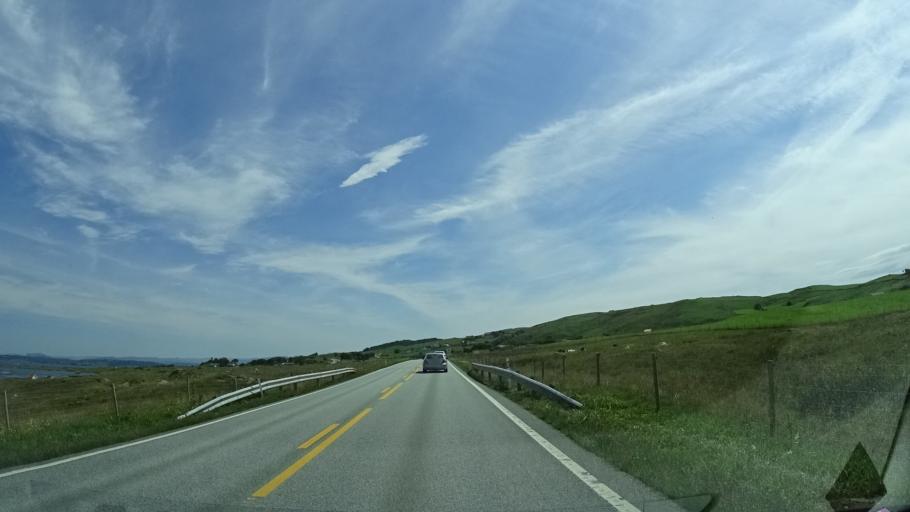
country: NO
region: Rogaland
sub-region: Rennesoy
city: Vikevag
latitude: 59.1285
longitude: 5.6181
